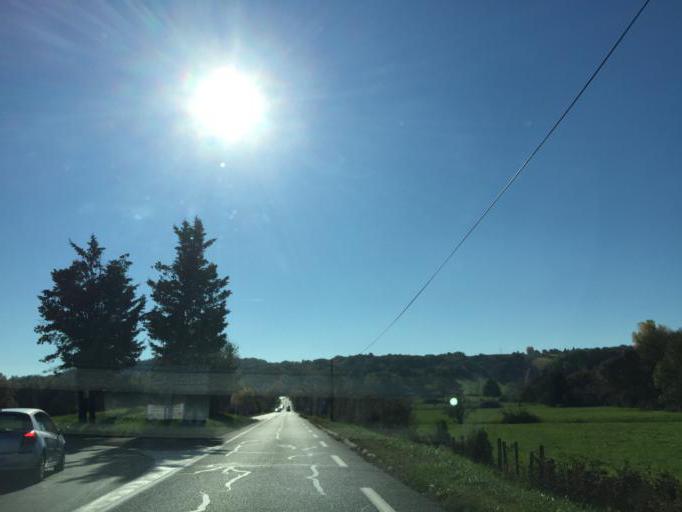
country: FR
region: Rhone-Alpes
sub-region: Departement du Rhone
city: Brignais
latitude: 45.6523
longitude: 4.7492
